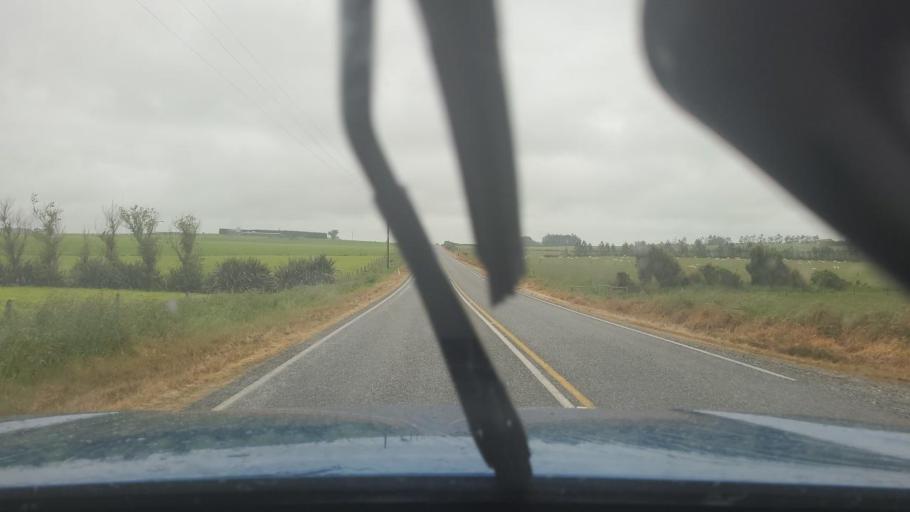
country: NZ
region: Southland
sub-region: Invercargill City
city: Invercargill
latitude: -46.4516
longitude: 168.5662
